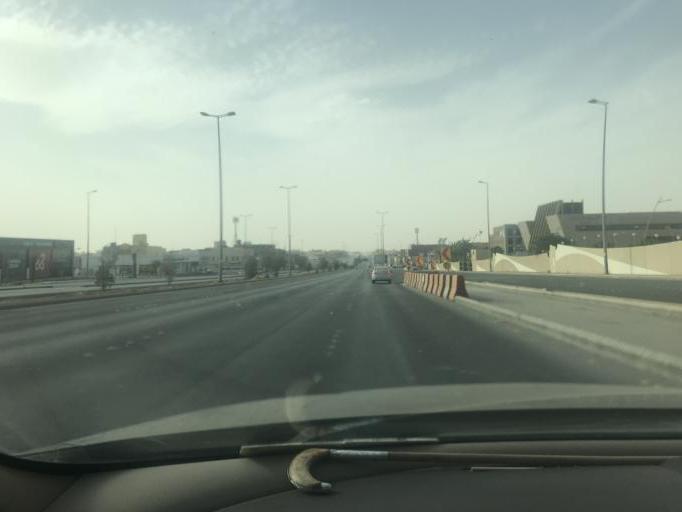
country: SA
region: Ar Riyad
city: Riyadh
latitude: 24.8247
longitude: 46.6845
